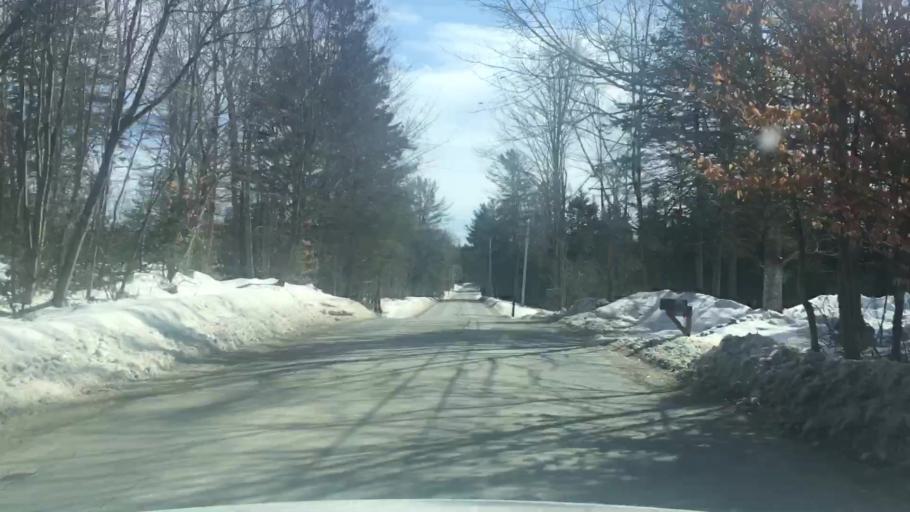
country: US
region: Maine
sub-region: Penobscot County
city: Holden
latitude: 44.7571
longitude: -68.6381
